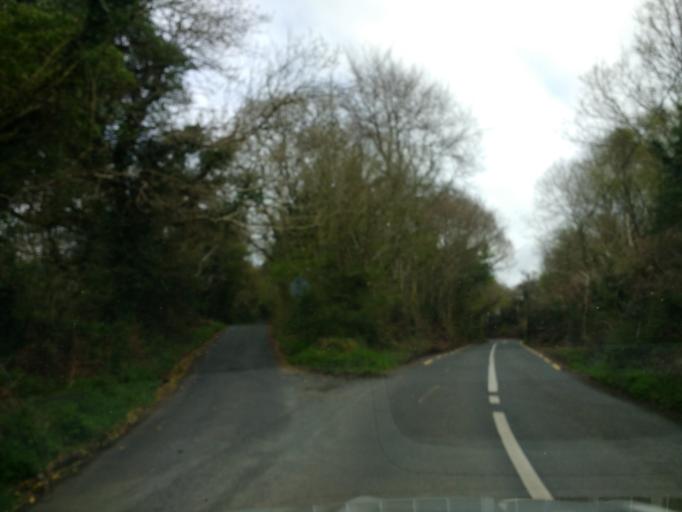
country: IE
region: Ulster
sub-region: County Donegal
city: Buncrana
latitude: 55.1280
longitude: -7.5290
